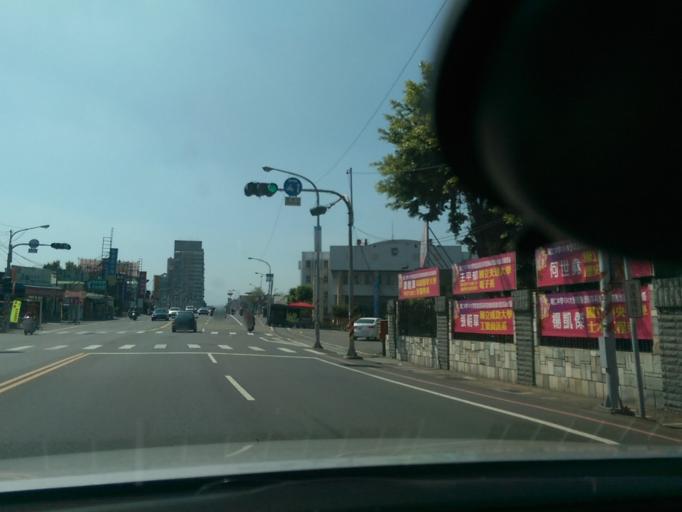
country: TW
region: Taiwan
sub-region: Chiayi
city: Jiayi Shi
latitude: 23.4612
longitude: 120.4571
